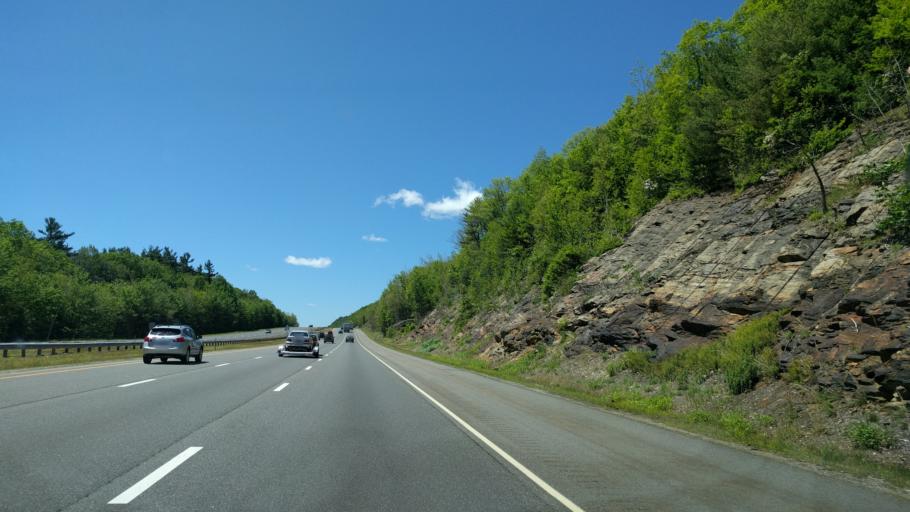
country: US
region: Massachusetts
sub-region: Hampden County
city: Holland
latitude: 42.0138
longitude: -72.1569
